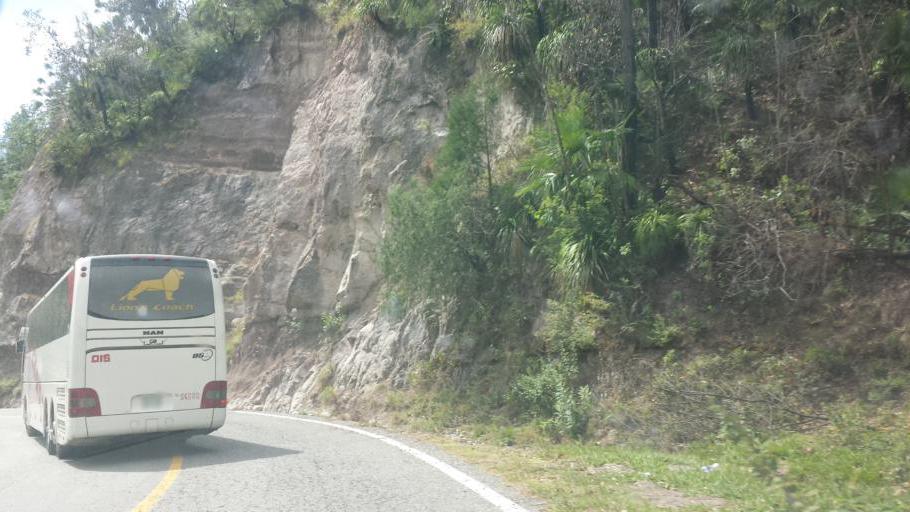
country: MX
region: Oaxaca
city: San Francisco Sola
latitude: 16.4512
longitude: -97.0332
